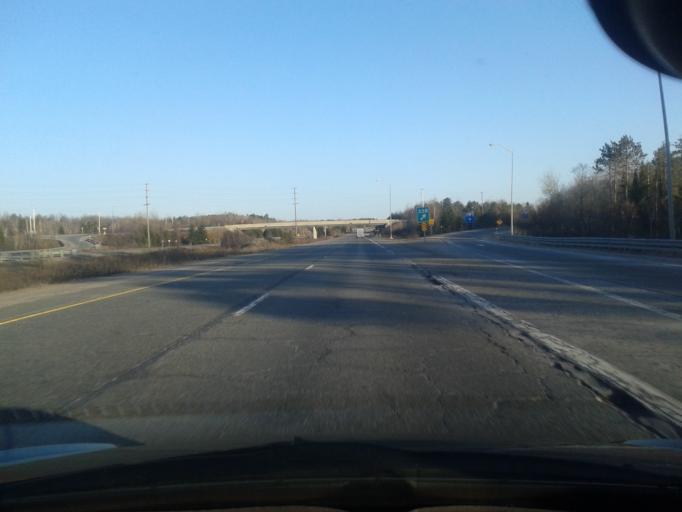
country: CA
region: Ontario
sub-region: Nipissing District
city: North Bay
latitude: 46.2665
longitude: -79.3948
